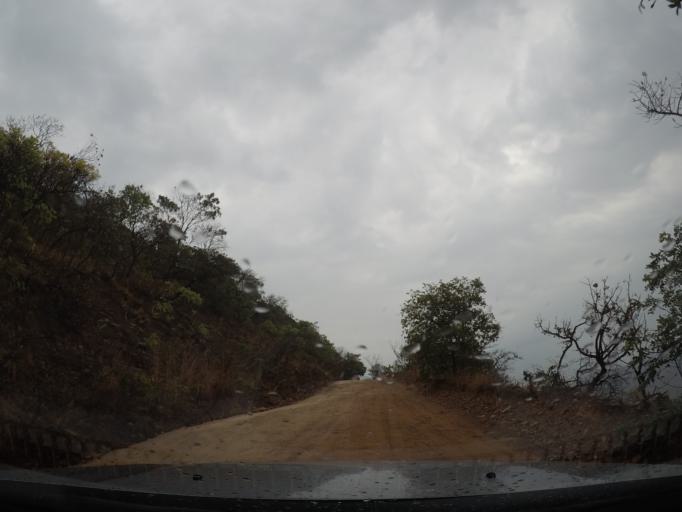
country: BR
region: Goias
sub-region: Pirenopolis
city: Pirenopolis
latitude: -15.8186
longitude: -48.9000
